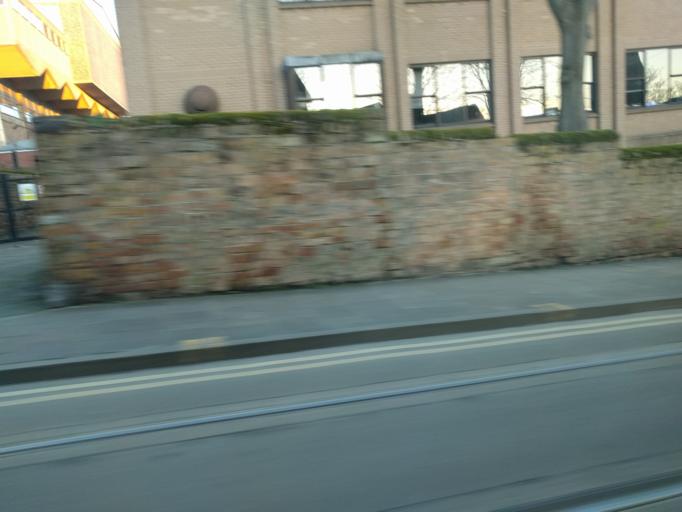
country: GB
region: England
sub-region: Nottingham
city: Nottingham
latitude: 52.9618
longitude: -1.1608
